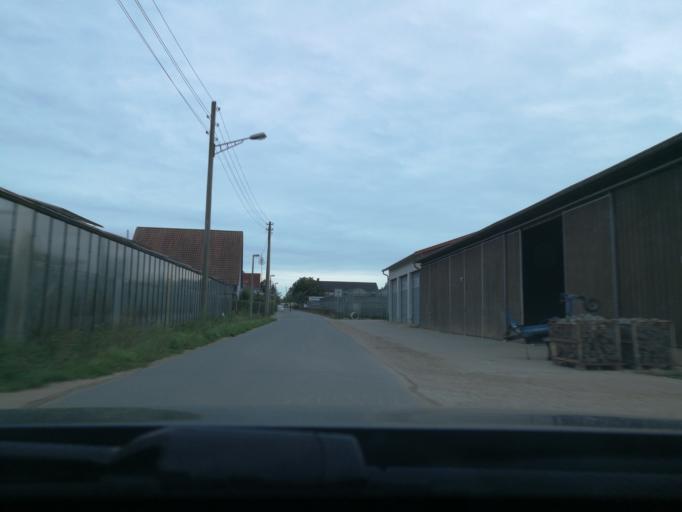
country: DE
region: Bavaria
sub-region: Regierungsbezirk Mittelfranken
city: Wetzendorf
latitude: 49.4723
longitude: 11.0417
